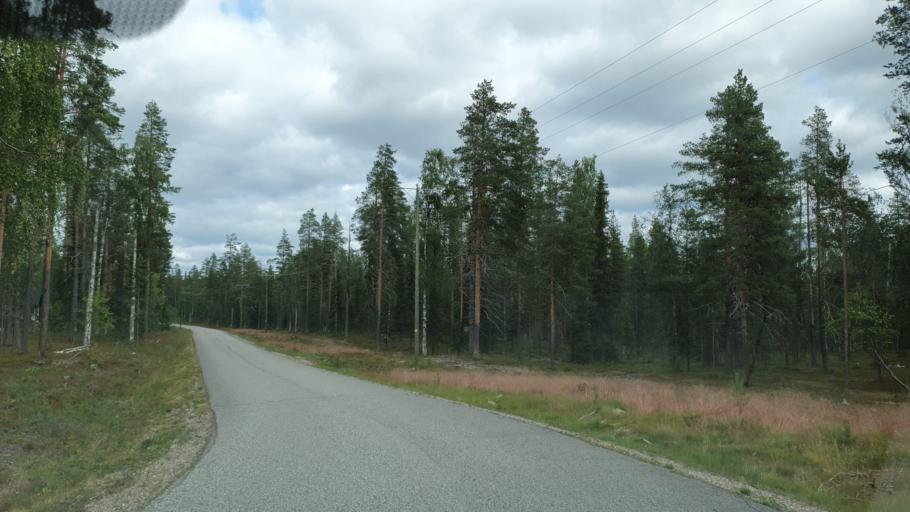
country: FI
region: Lapland
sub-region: Tunturi-Lappi
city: Kolari
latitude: 67.5470
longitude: 24.2748
